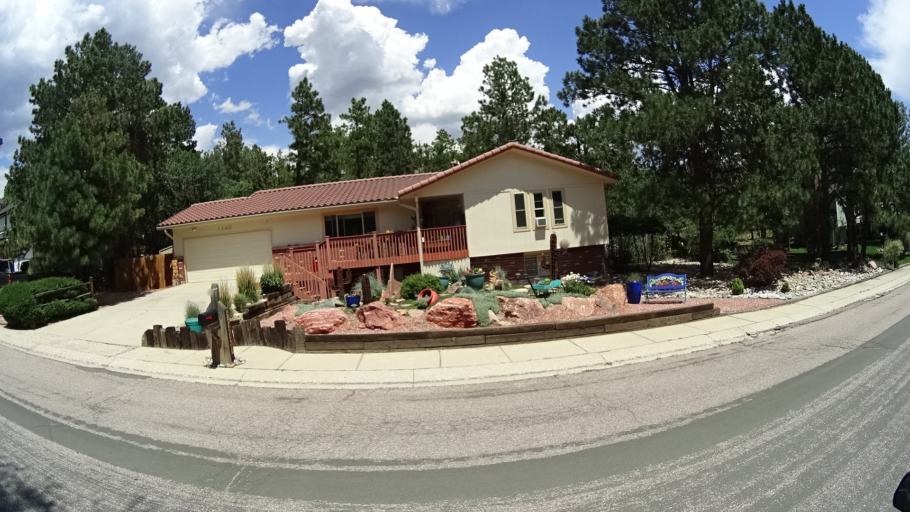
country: US
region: Colorado
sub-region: El Paso County
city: Air Force Academy
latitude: 38.9376
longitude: -104.8483
